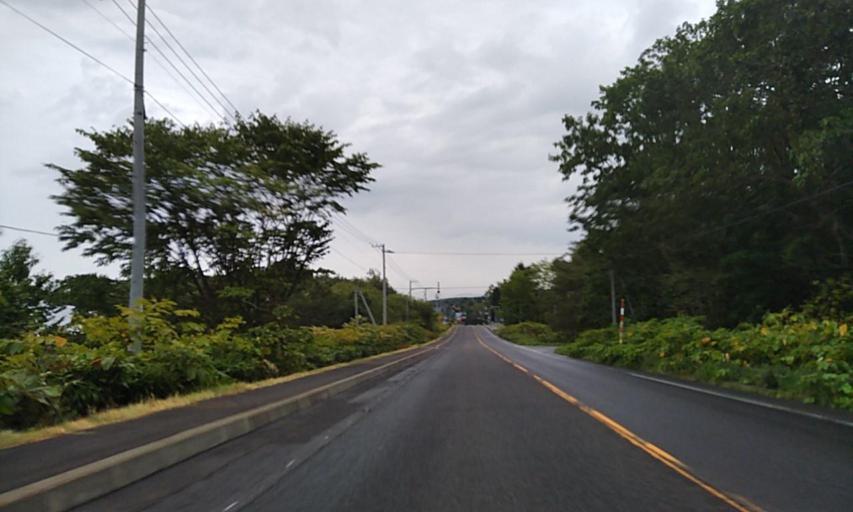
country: JP
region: Hokkaido
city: Mombetsu
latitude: 44.5214
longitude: 143.0544
